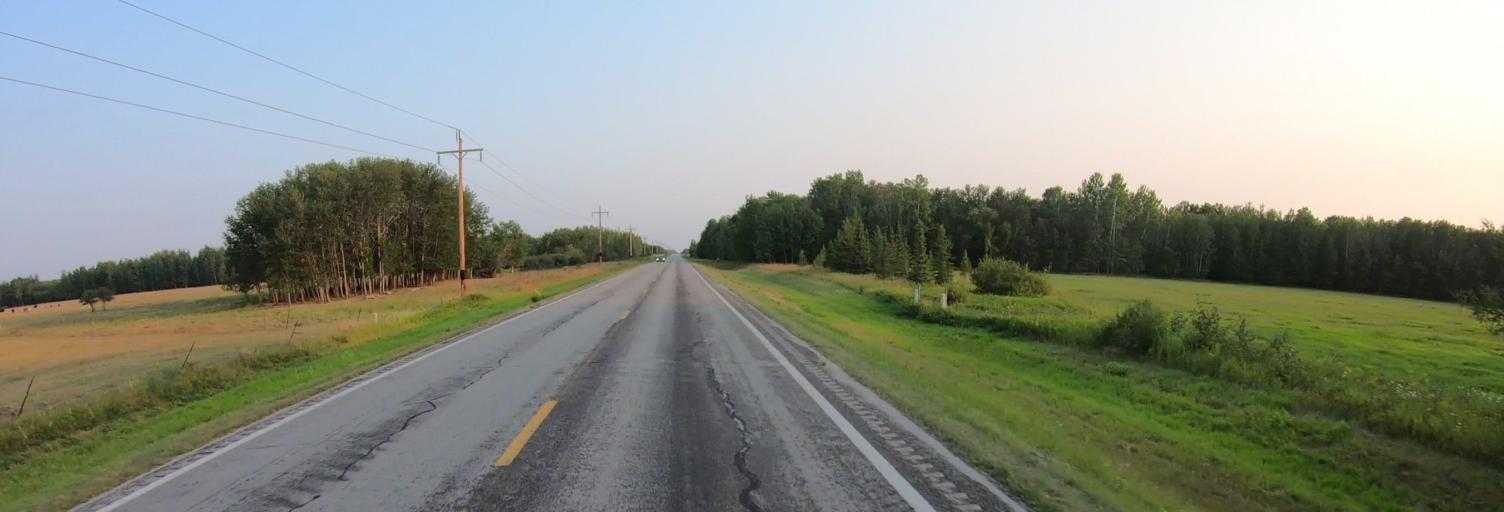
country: US
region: Minnesota
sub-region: Roseau County
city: Warroad
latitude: 48.8270
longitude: -95.3308
